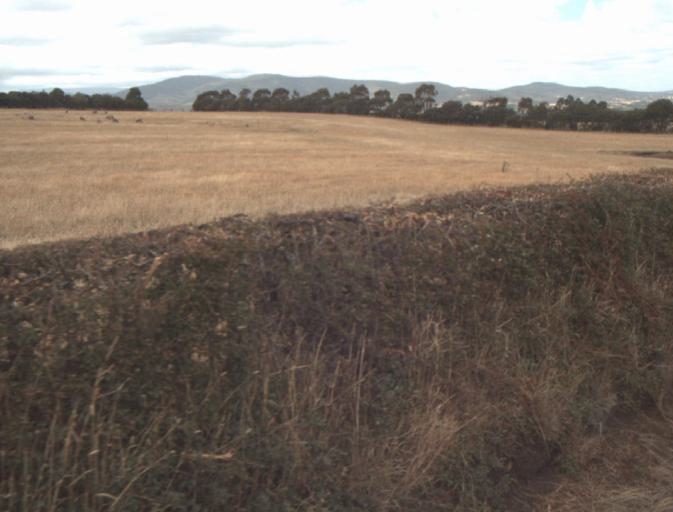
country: AU
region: Tasmania
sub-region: Northern Midlands
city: Evandale
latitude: -41.5222
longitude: 147.2641
